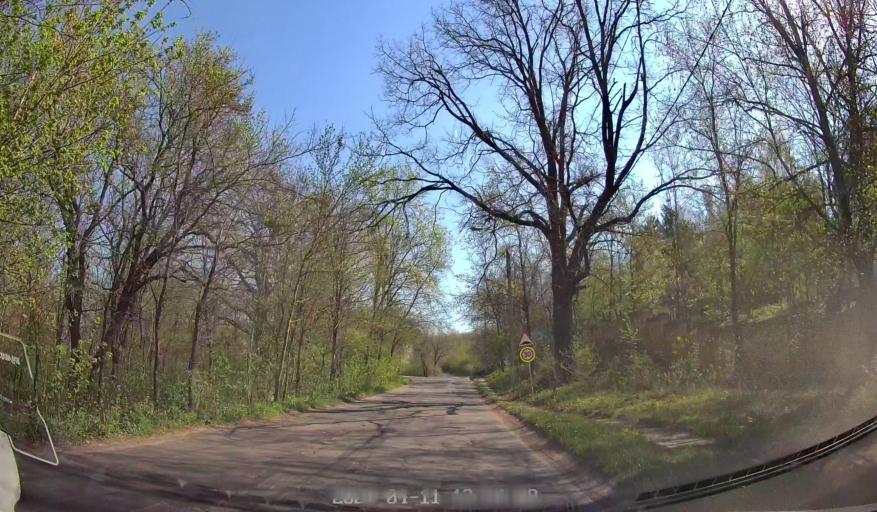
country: MD
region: Chisinau
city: Vadul lui Voda
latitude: 47.0760
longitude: 29.1002
